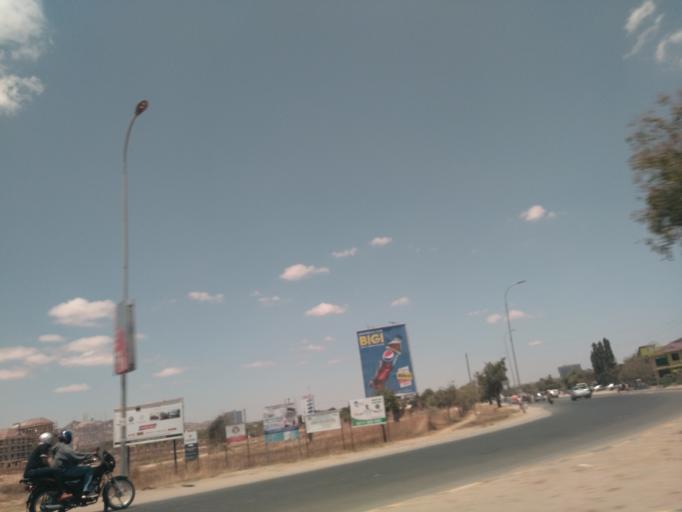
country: TZ
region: Dodoma
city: Dodoma
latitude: -6.1751
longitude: 35.7632
